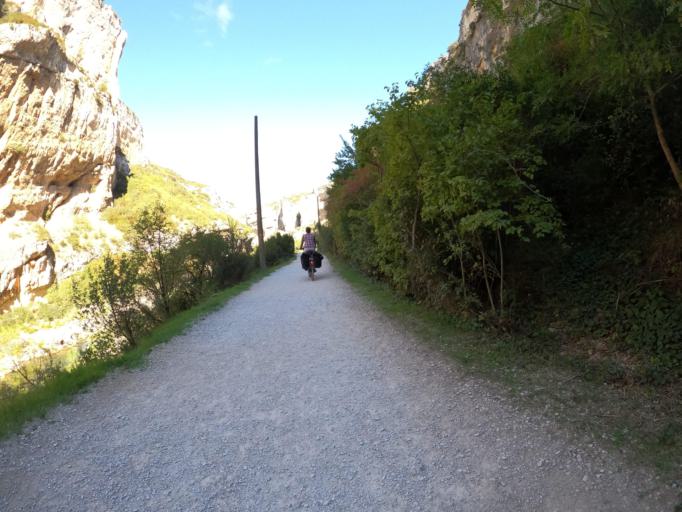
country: ES
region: Navarre
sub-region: Provincia de Navarra
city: Lumbier
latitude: 42.6269
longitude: -1.3018
